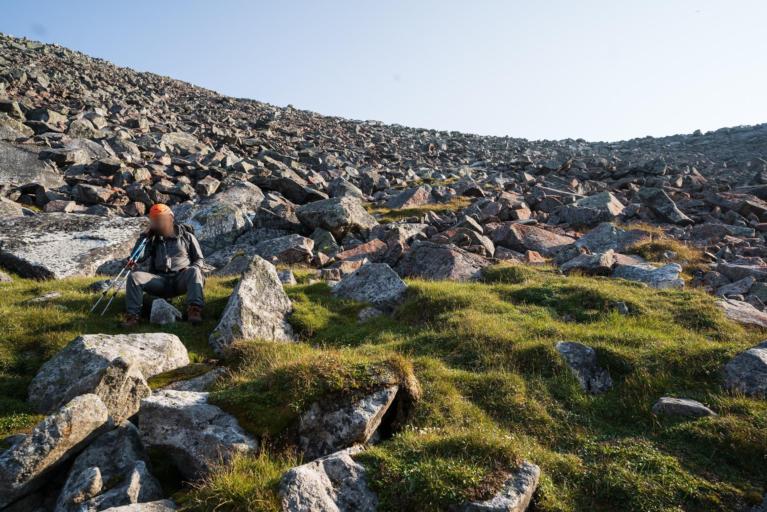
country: RU
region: Transbaikal Territory
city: Kuanda
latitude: 56.7925
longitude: 116.8158
